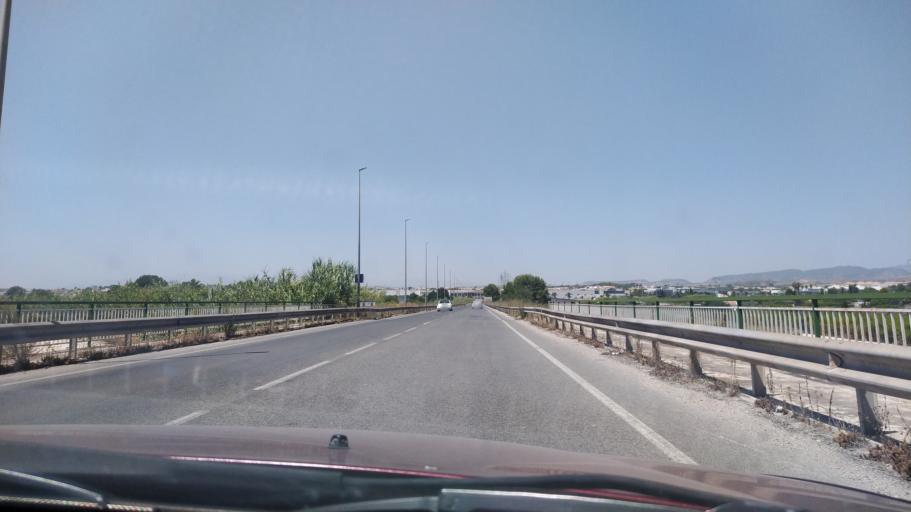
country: ES
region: Murcia
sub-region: Murcia
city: Lorqui
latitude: 38.0854
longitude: -1.2579
